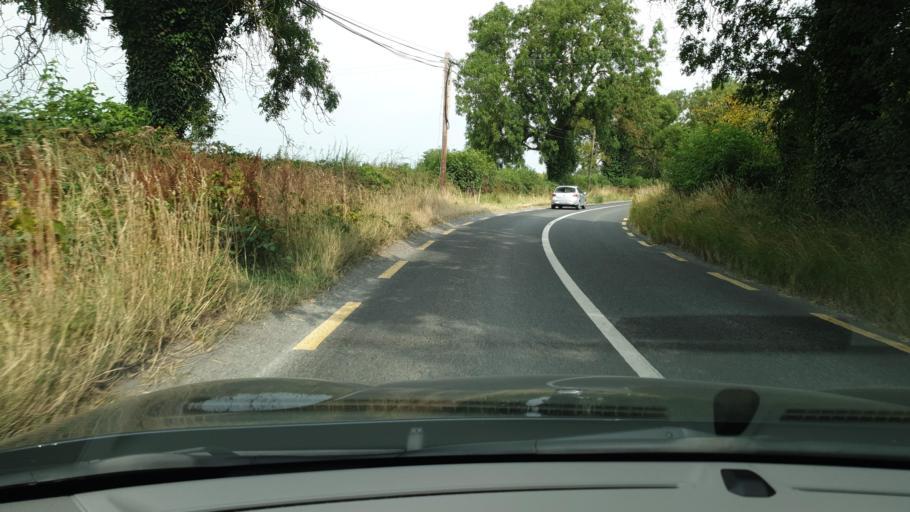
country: IE
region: Leinster
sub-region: An Mhi
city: Athboy
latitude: 53.6571
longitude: -6.8952
